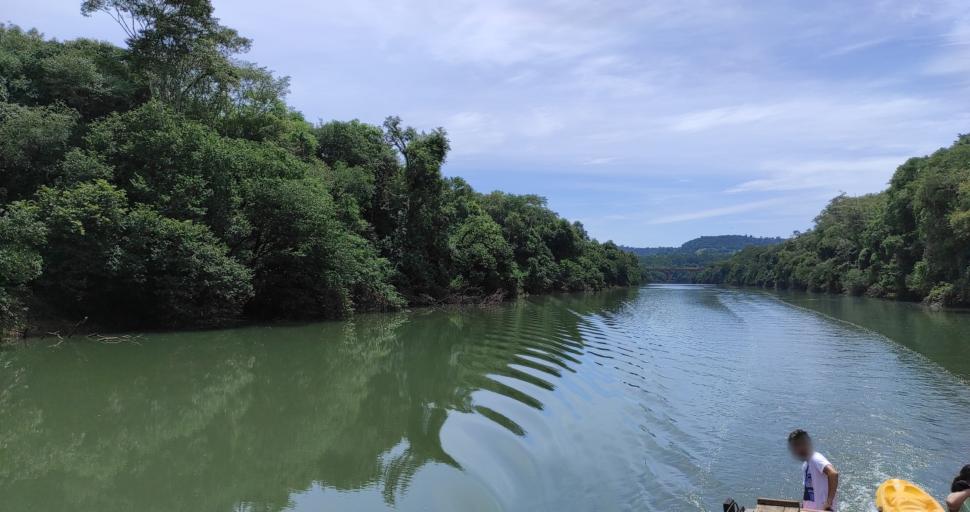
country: AR
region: Misiones
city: El Soberbio
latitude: -27.2831
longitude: -54.2063
